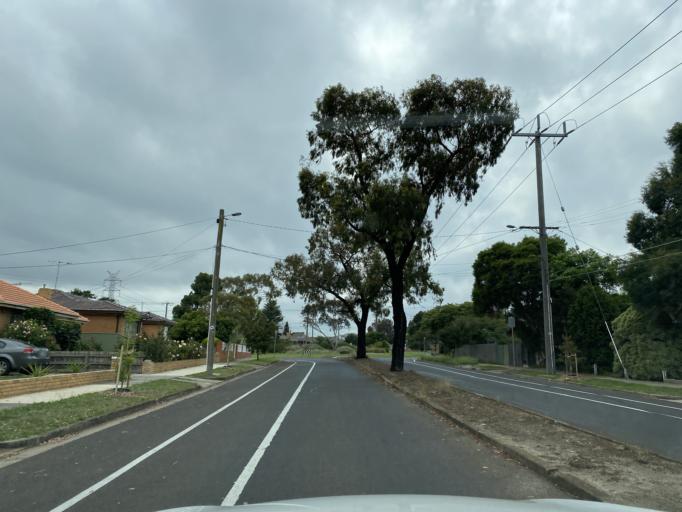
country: AU
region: Victoria
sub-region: Darebin
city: Reservoir
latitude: -37.7011
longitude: 145.0032
